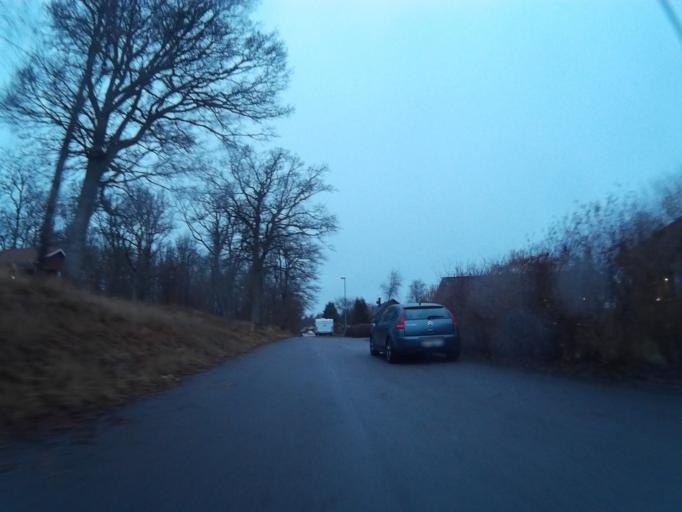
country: SE
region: Kronoberg
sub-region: Vaxjo Kommun
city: Vaexjoe
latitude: 56.9107
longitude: 14.7418
